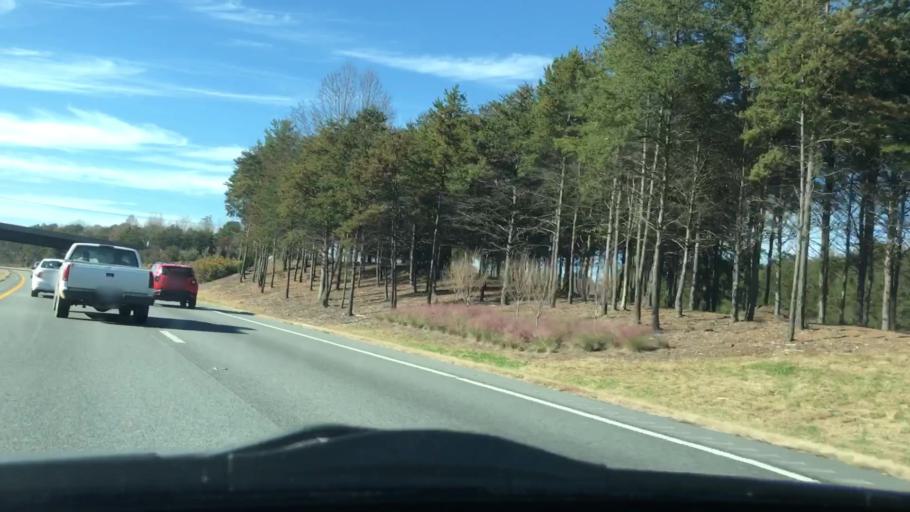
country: US
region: North Carolina
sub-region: Davidson County
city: Wallburg
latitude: 36.0261
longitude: -80.0567
